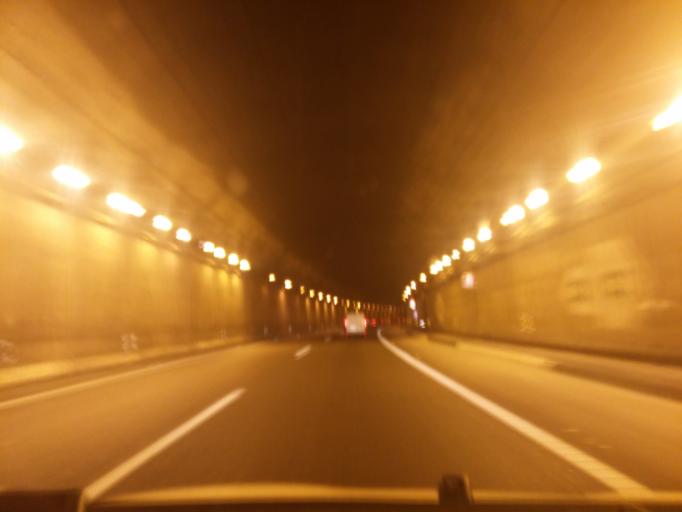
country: ES
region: Valencia
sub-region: Provincia de Alicante
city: San Juan de Alicante
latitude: 38.4033
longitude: -0.4480
